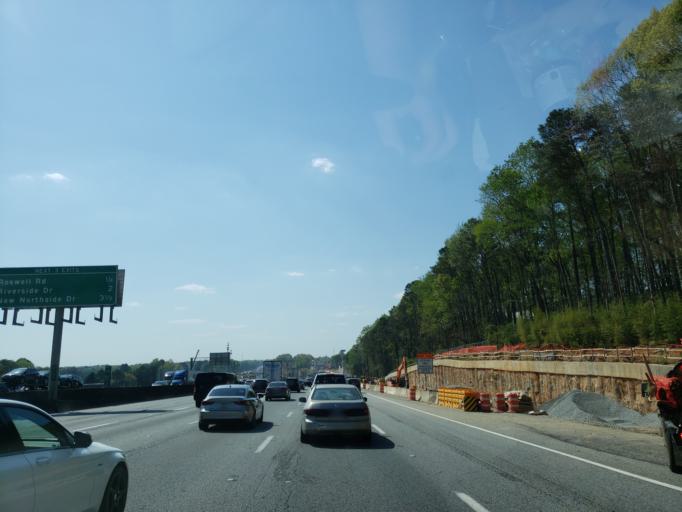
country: US
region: Georgia
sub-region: Fulton County
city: Sandy Springs
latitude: 33.9124
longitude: -84.3704
